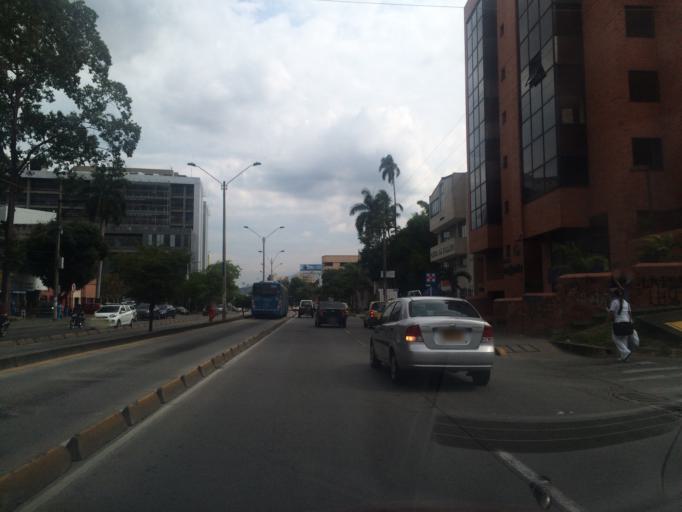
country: CO
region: Valle del Cauca
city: Cali
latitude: 3.4283
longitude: -76.5451
